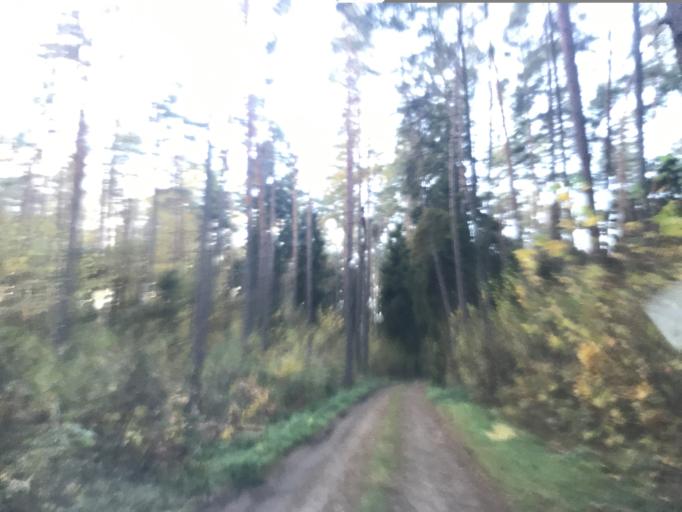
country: PL
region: Warmian-Masurian Voivodeship
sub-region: Powiat dzialdowski
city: Lidzbark
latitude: 53.2299
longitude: 19.7941
